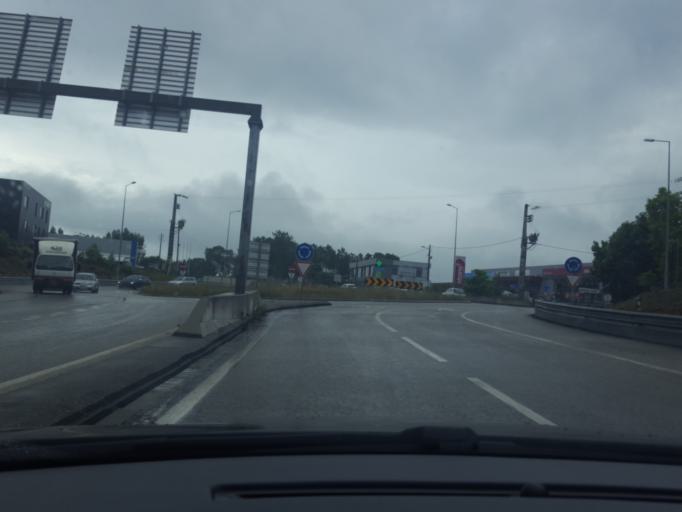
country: PT
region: Leiria
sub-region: Leiria
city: Leiria
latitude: 39.7360
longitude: -8.7692
